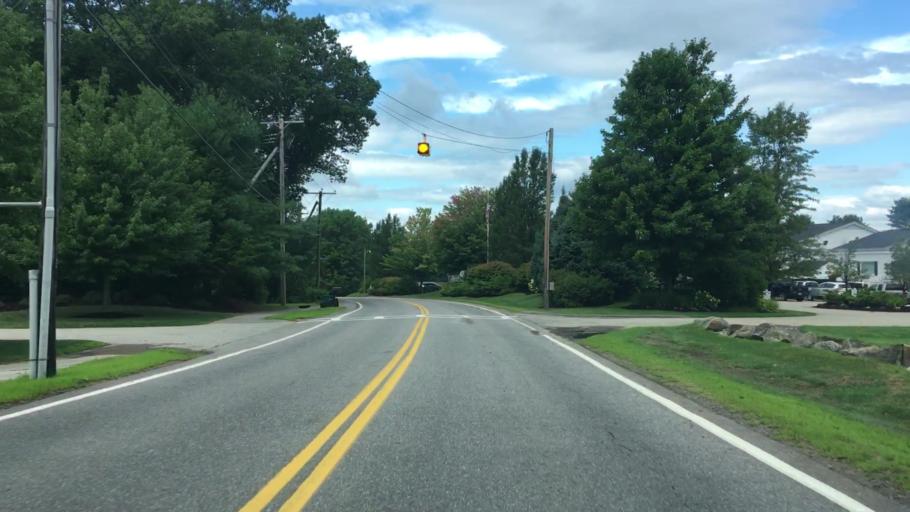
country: US
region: New Hampshire
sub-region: Belknap County
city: Laconia
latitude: 43.5614
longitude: -71.4756
